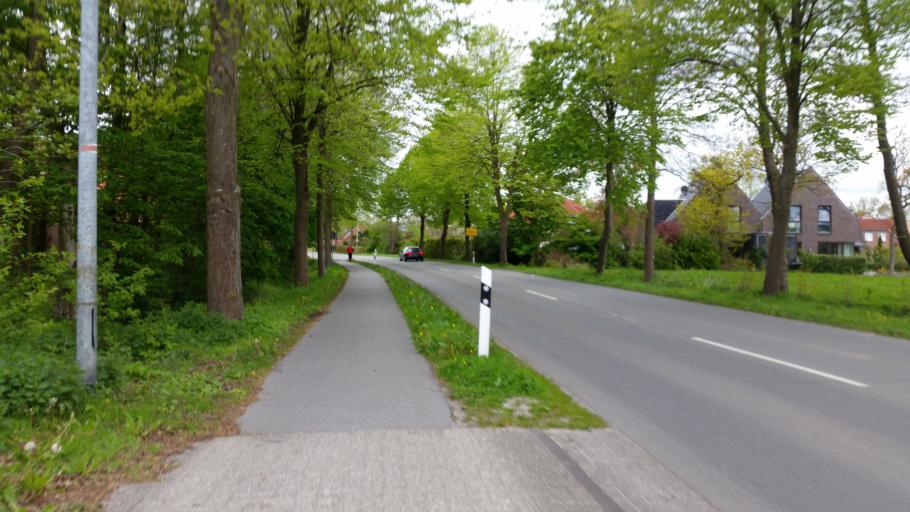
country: DE
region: Lower Saxony
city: Aurich
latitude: 53.4779
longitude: 7.4559
